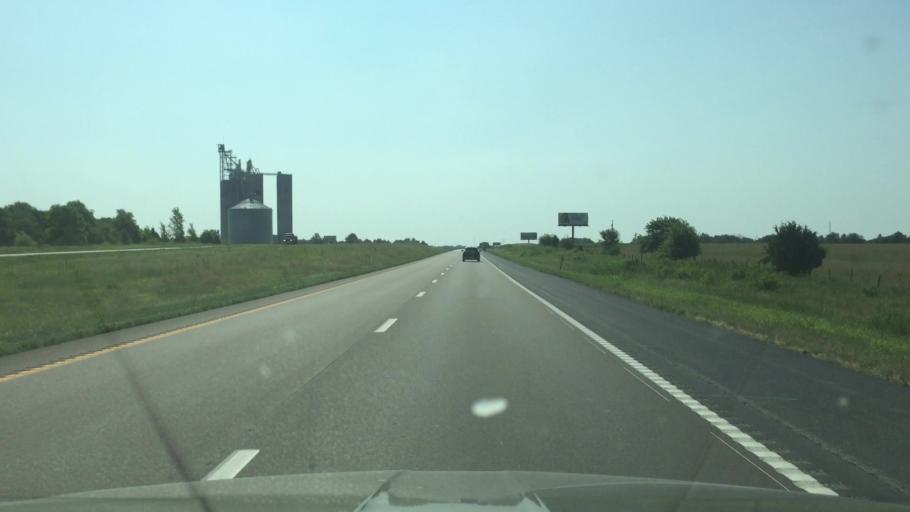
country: US
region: Missouri
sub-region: Pettis County
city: La Monte
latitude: 38.7520
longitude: -93.3527
